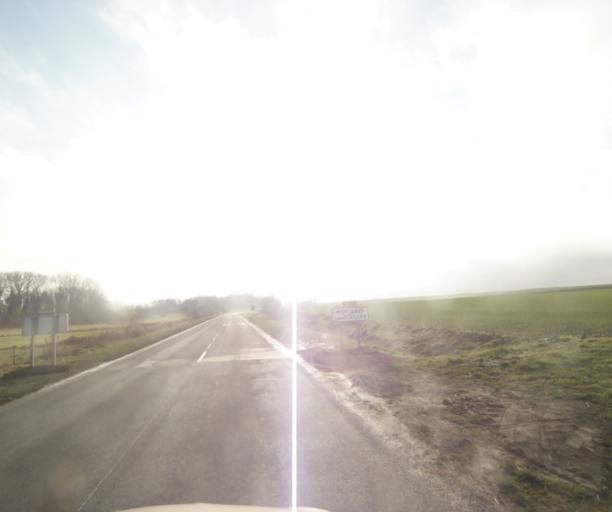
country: FR
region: Nord-Pas-de-Calais
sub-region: Departement du Nord
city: Thiant
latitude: 50.2800
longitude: 3.4526
